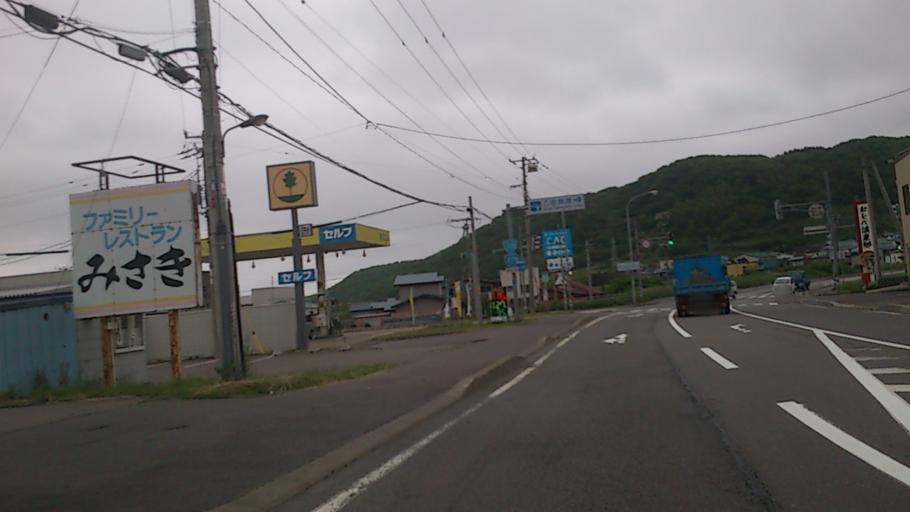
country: JP
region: Hokkaido
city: Kamiiso
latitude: 41.9751
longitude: 140.1382
